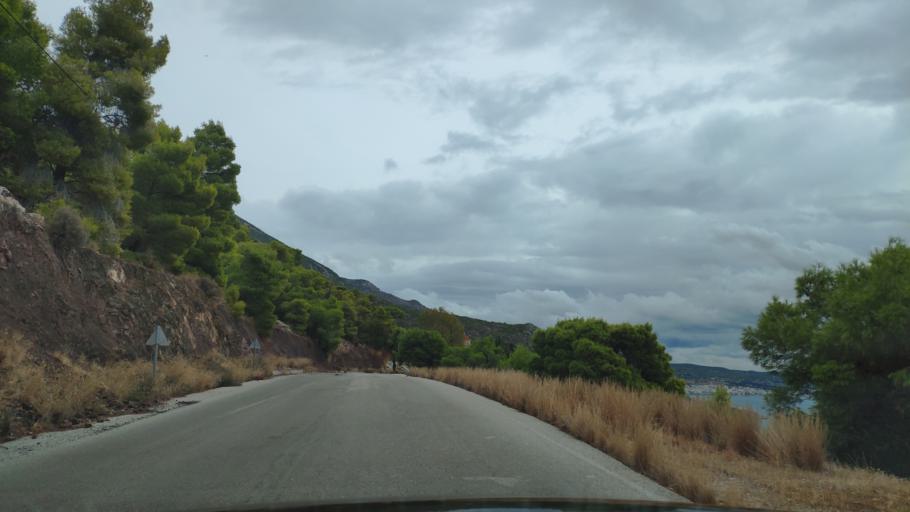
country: GR
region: Peloponnese
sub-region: Nomos Korinthias
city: Perachora
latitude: 38.0033
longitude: 22.9339
